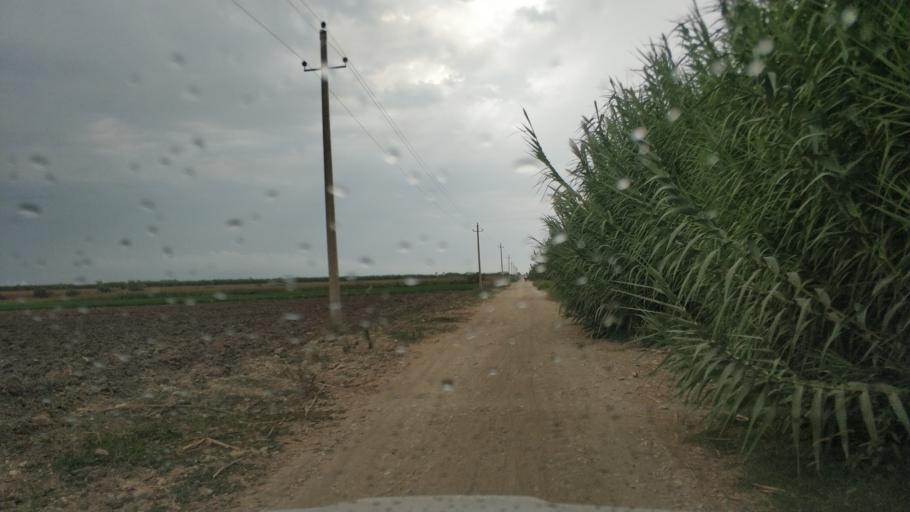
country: AL
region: Fier
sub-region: Rrethi i Fierit
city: Dermenas
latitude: 40.7160
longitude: 19.4542
